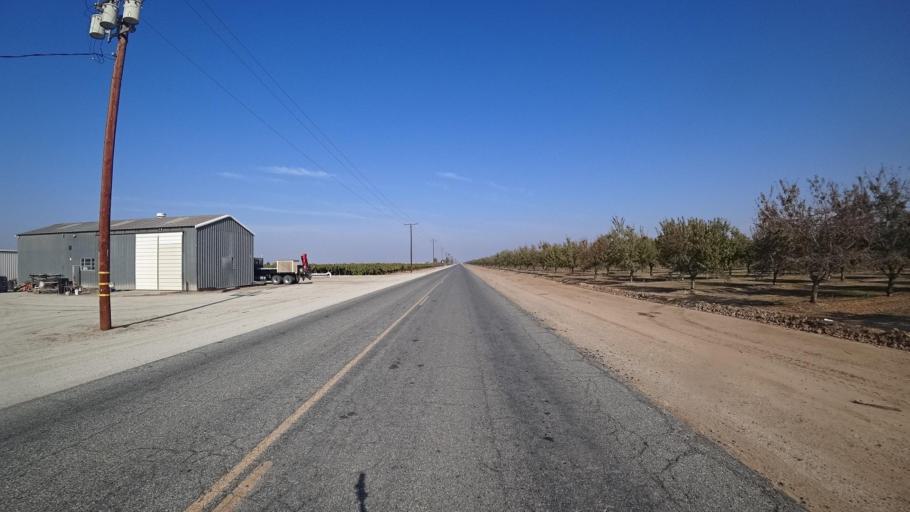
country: US
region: California
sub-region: Kern County
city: McFarland
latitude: 35.6824
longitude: -119.2048
